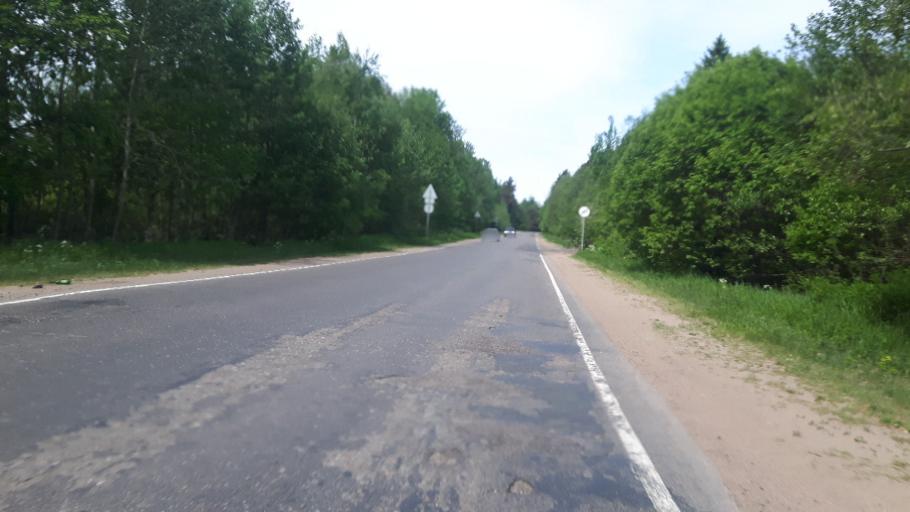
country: RU
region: Leningrad
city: Ust'-Luga
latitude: 59.6463
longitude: 28.2670
